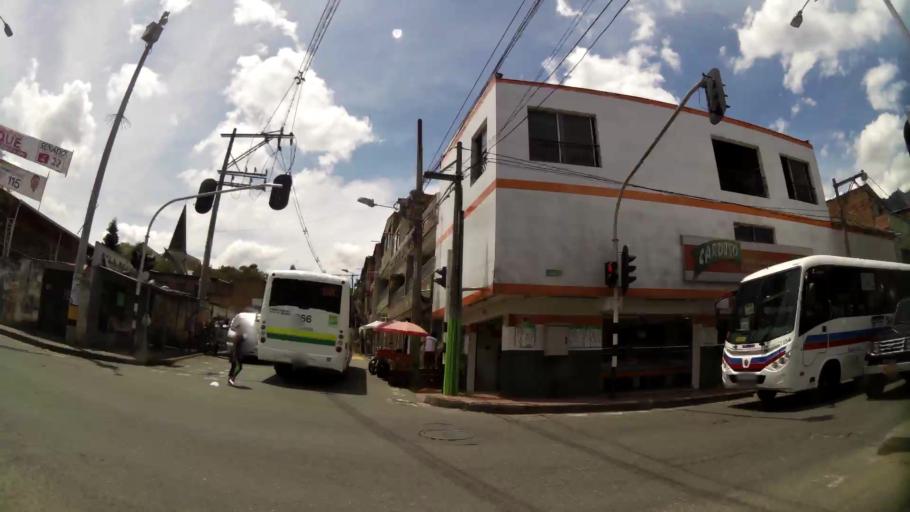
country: CO
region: Antioquia
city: Bello
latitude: 6.3421
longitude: -75.5671
